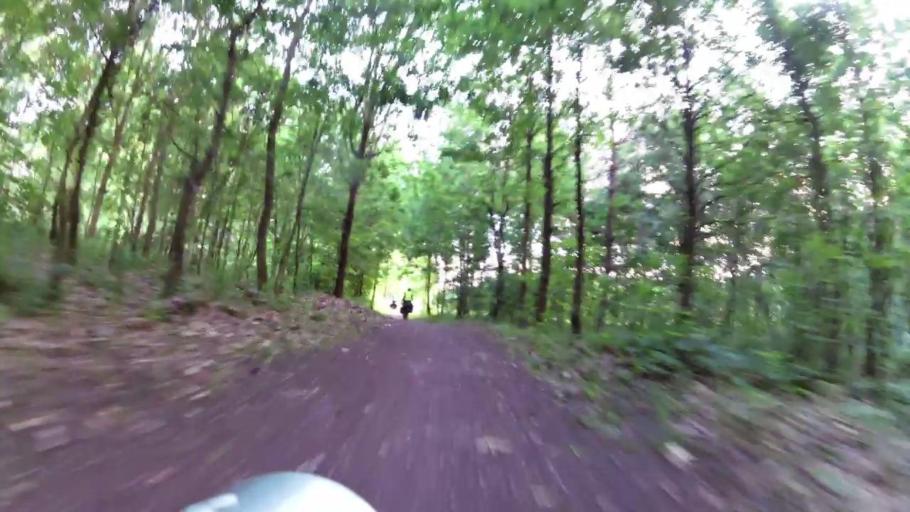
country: PL
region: Kujawsko-Pomorskie
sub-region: Powiat bydgoski
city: Dabrowa Chelminska
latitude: 53.1705
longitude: 18.2637
